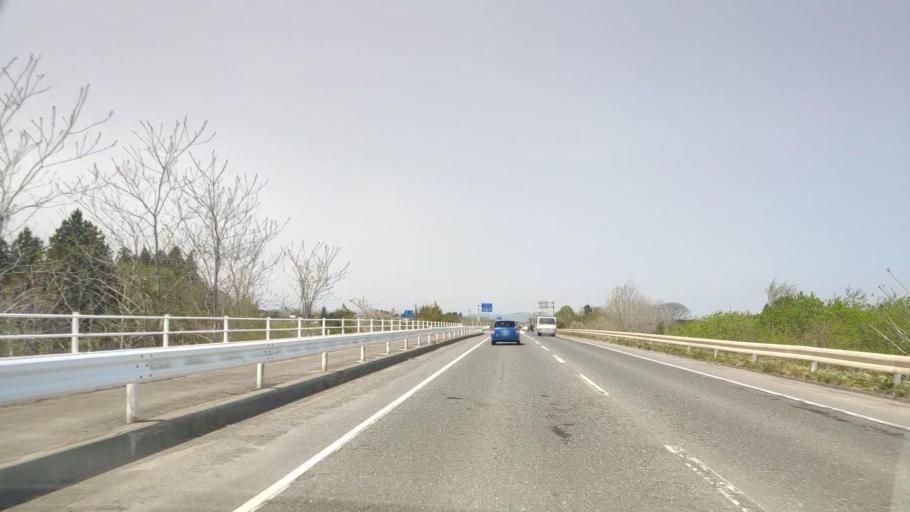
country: JP
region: Aomori
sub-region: Misawa Shi
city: Inuotose
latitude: 40.6315
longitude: 141.2476
